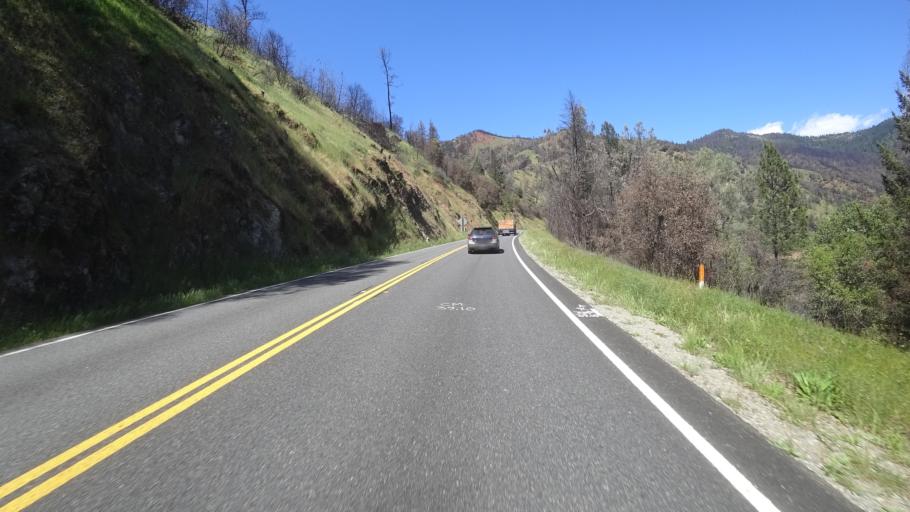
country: US
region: California
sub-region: Trinity County
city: Weaverville
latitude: 40.7627
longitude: -123.0974
